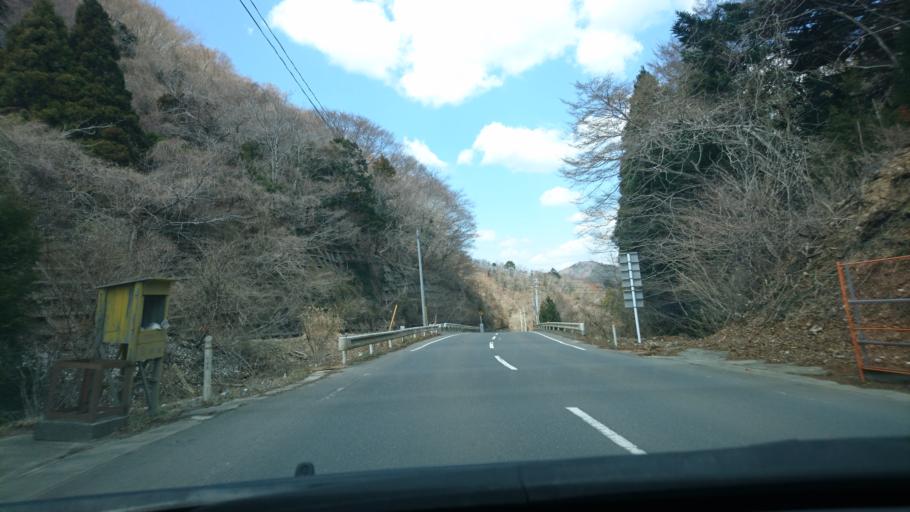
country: JP
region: Miyagi
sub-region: Oshika Gun
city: Onagawa Cho
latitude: 38.4555
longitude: 141.4867
